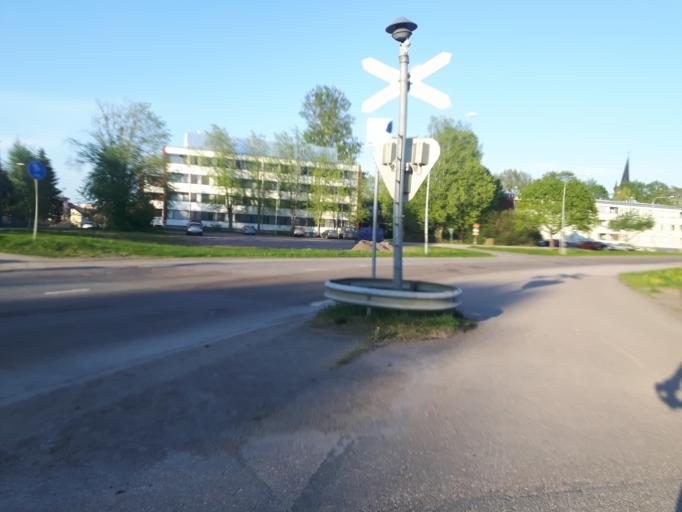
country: FI
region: Uusimaa
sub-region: Loviisa
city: Lovisa
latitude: 60.4573
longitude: 26.2162
